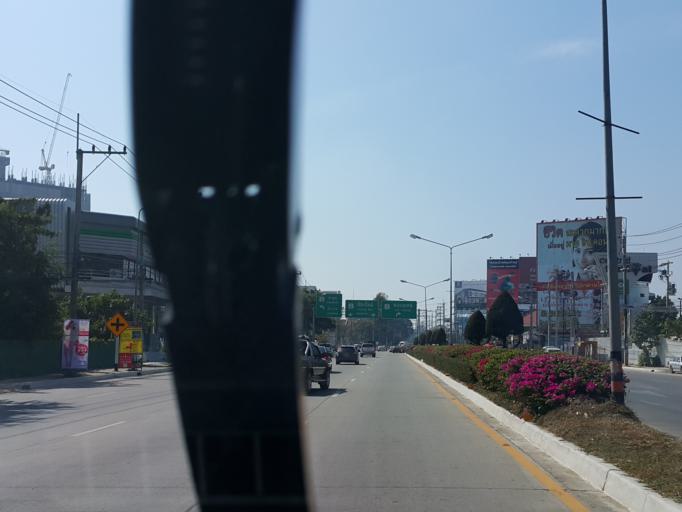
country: TH
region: Chiang Mai
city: Chiang Mai
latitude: 18.8056
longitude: 99.0209
